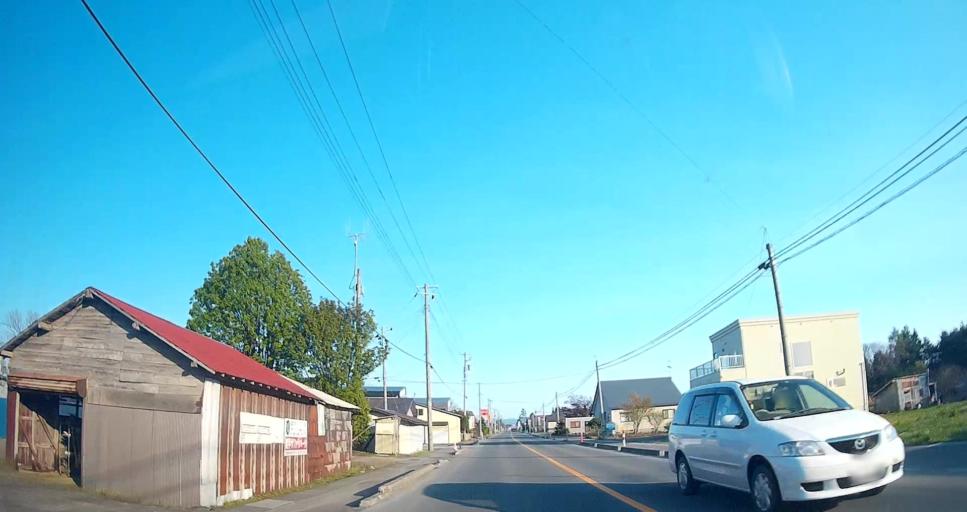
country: JP
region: Aomori
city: Mutsu
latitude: 41.2679
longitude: 141.2205
